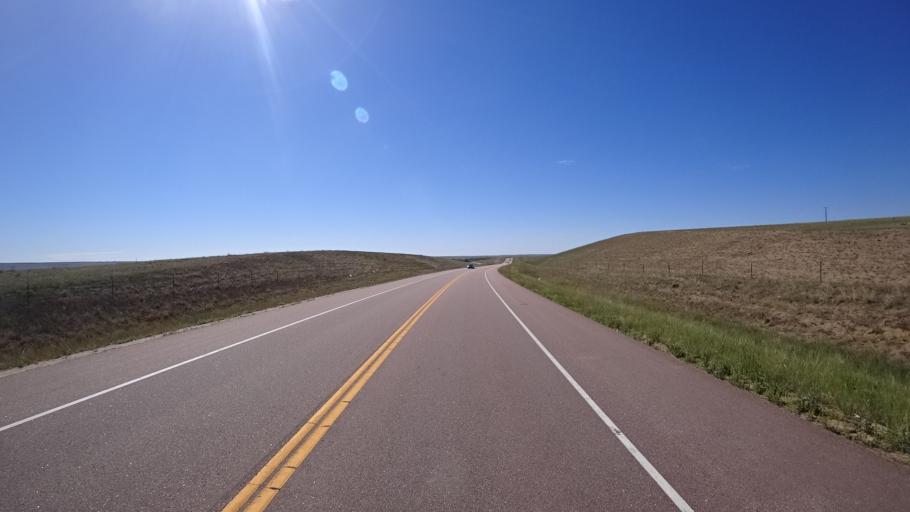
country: US
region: Colorado
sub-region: El Paso County
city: Cimarron Hills
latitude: 38.8019
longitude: -104.6625
